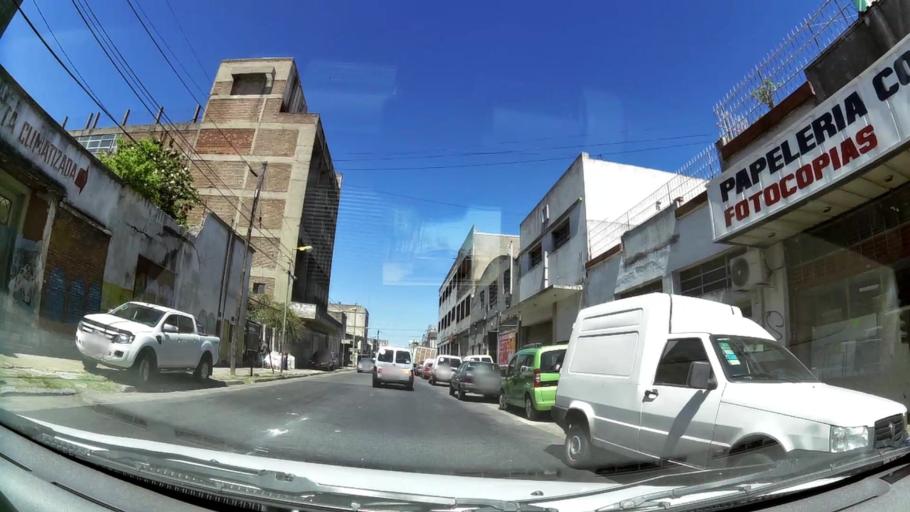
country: AR
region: Buenos Aires
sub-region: Partido de General San Martin
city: General San Martin
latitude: -34.5886
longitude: -58.5281
